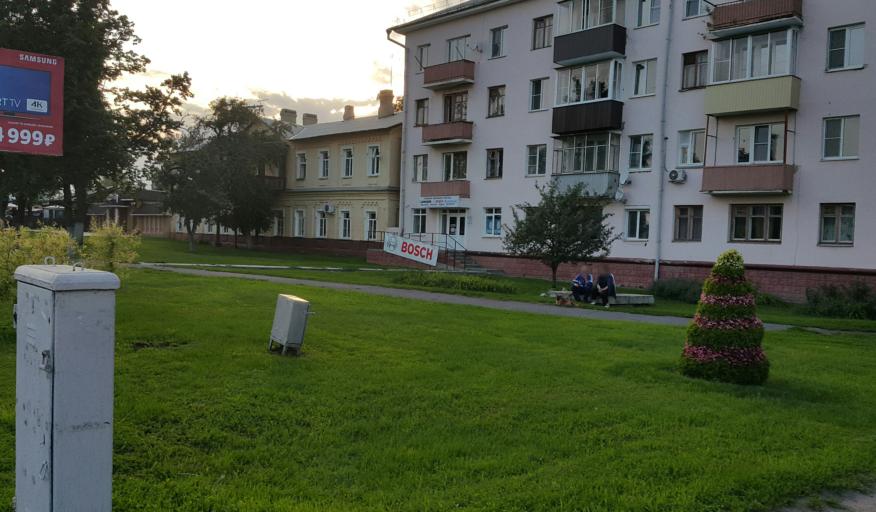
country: RU
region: Tambov
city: Tambov
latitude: 52.7192
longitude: 41.4292
